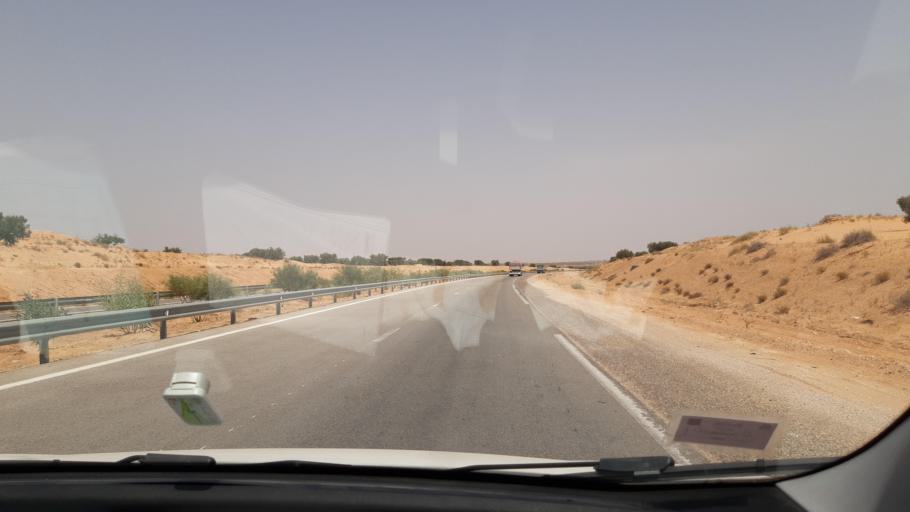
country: TN
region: Safaqis
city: Bi'r `Ali Bin Khalifah
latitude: 34.5271
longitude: 10.0846
